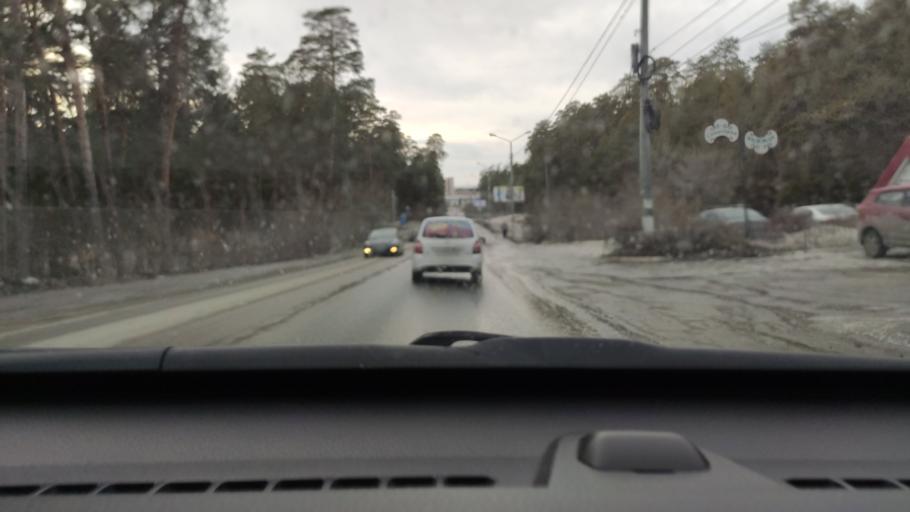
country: RU
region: Samara
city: Tol'yatti
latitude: 53.4765
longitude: 49.3353
